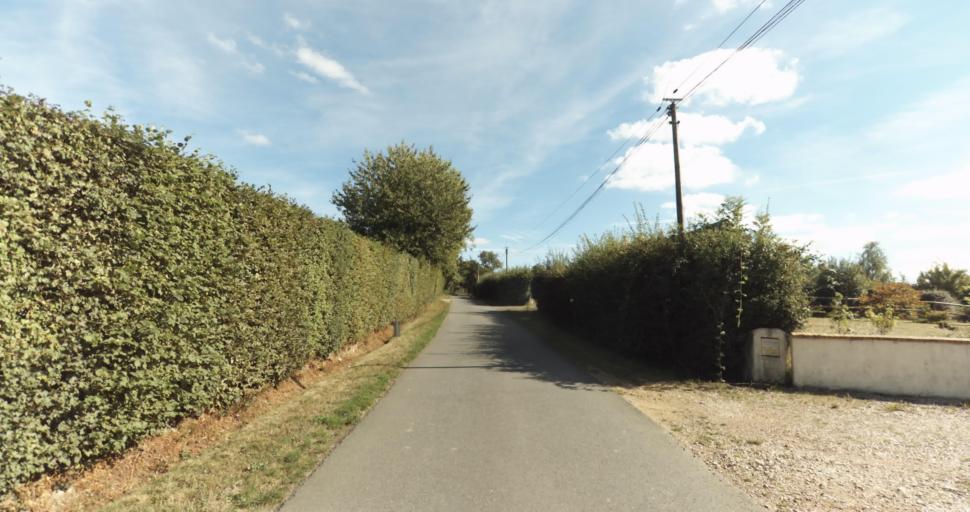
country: FR
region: Lower Normandy
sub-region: Departement de l'Orne
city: Vimoutiers
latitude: 48.9186
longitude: 0.1444
